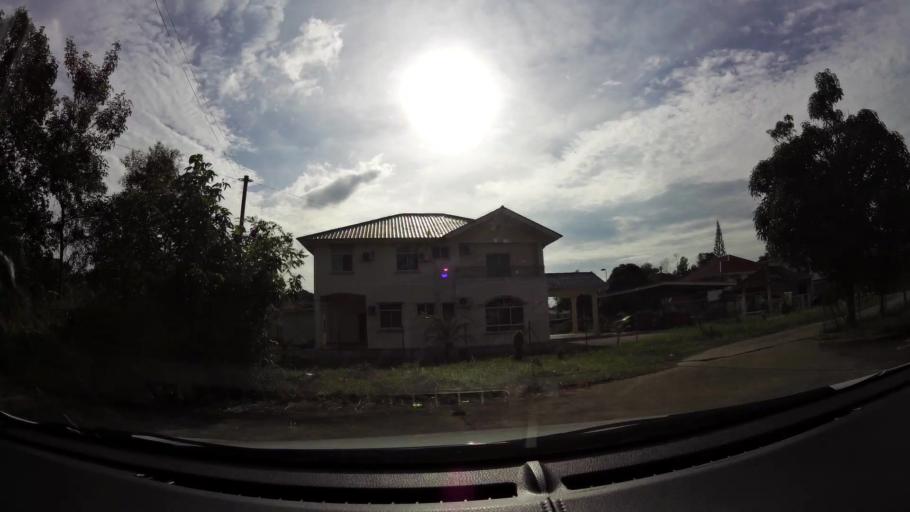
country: BN
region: Brunei and Muara
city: Bandar Seri Begawan
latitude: 4.9087
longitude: 114.8917
